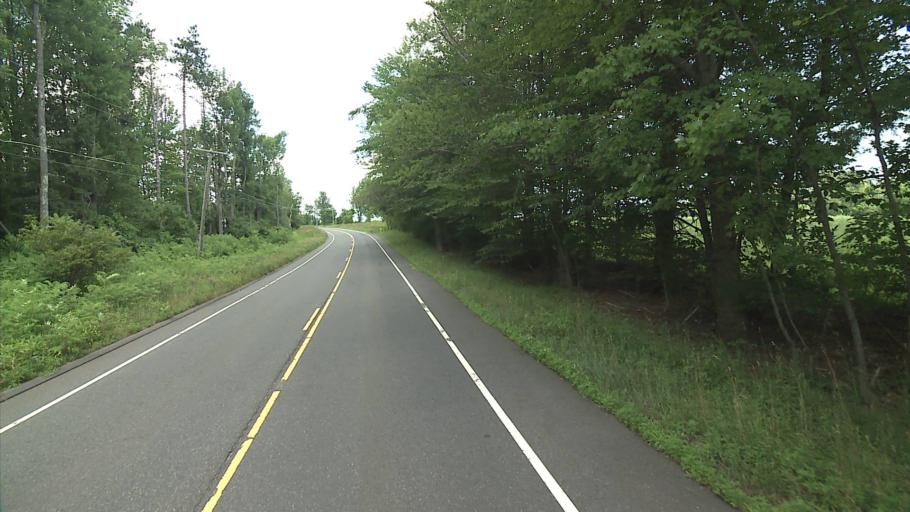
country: US
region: Massachusetts
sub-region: Hampden County
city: Granville
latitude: 42.0166
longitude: -72.9687
